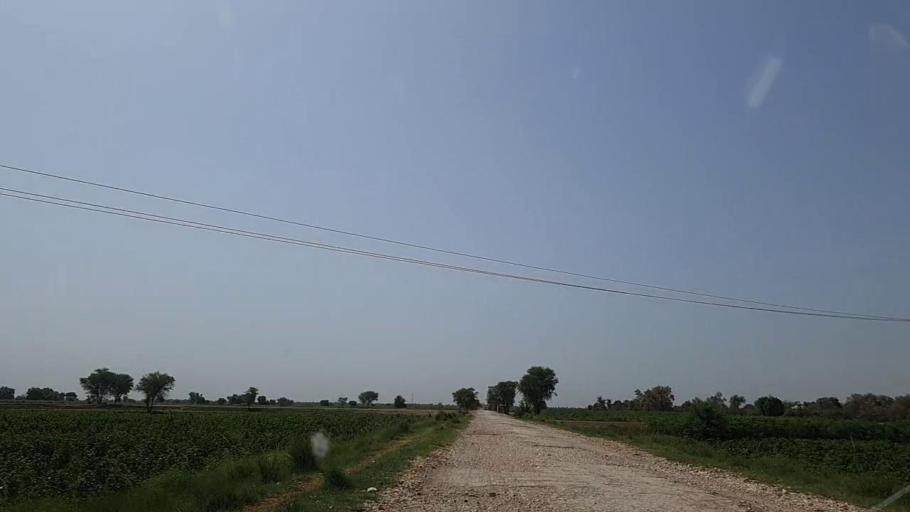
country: PK
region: Sindh
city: Naushahro Firoz
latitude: 26.8470
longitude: 68.0121
